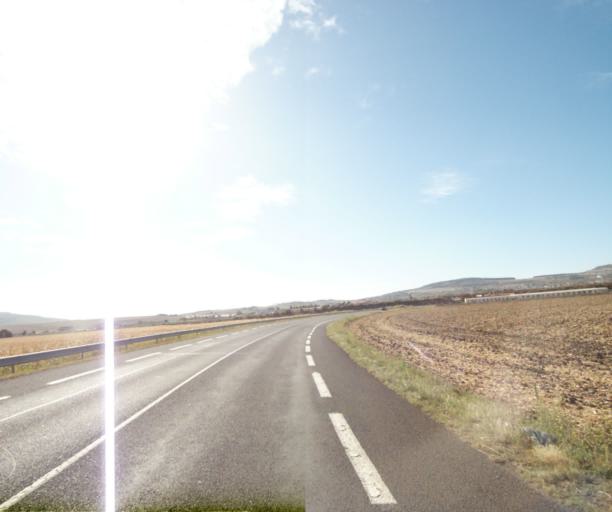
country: FR
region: Auvergne
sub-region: Departement du Puy-de-Dome
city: Malintrat
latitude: 45.7883
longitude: 3.2043
